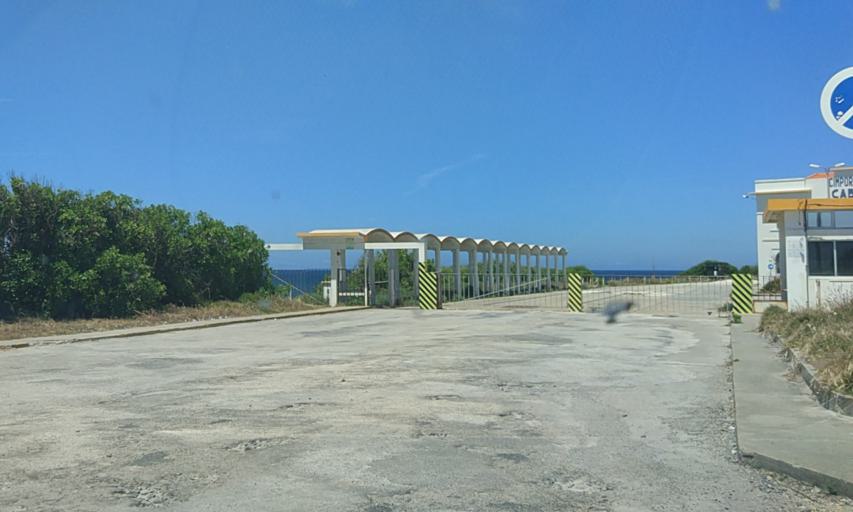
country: PT
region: Coimbra
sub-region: Figueira da Foz
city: Buarcos
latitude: 40.1791
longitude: -8.9060
